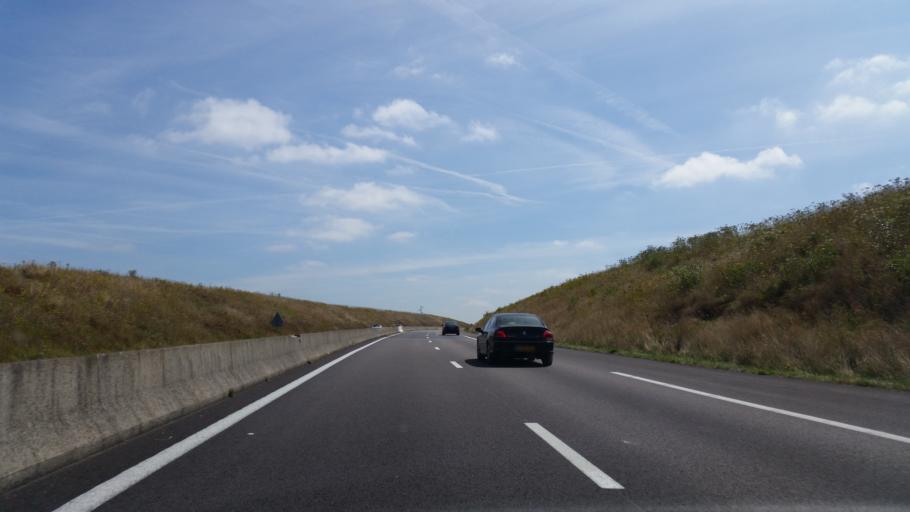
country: FR
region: Haute-Normandie
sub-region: Departement de la Seine-Maritime
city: Gaillefontaine
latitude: 49.7418
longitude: 1.5950
